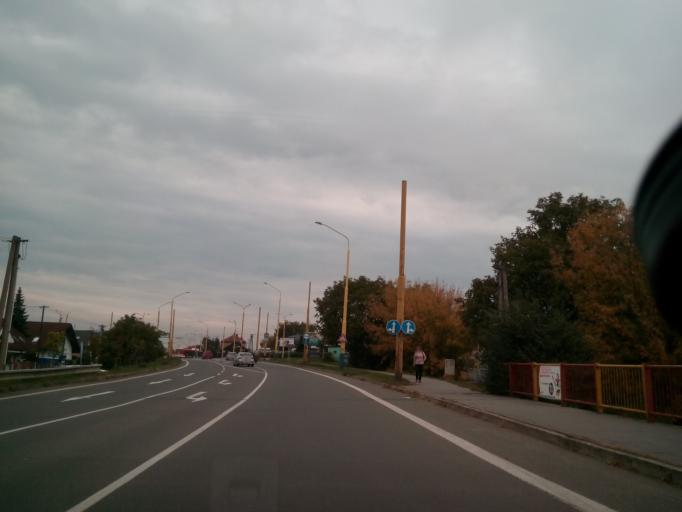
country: SK
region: Presovsky
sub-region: Okres Presov
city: Presov
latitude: 48.9763
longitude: 21.2639
